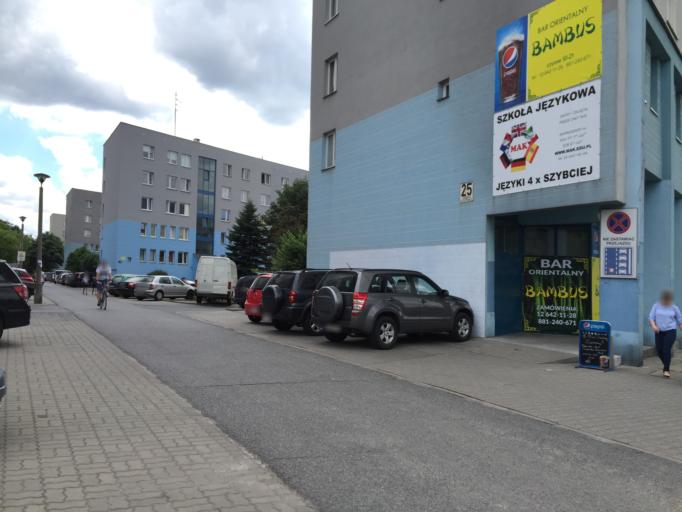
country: PL
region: Lesser Poland Voivodeship
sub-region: Powiat wielicki
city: Kokotow
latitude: 50.0707
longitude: 20.0375
